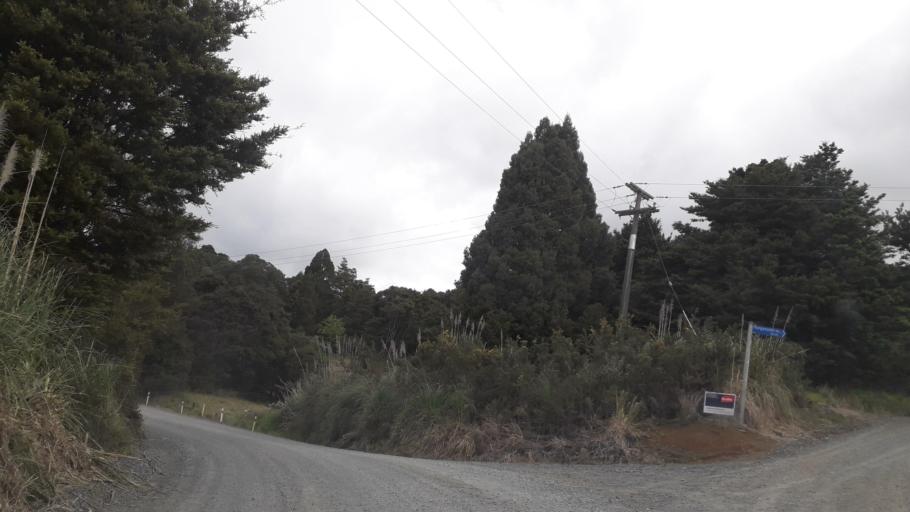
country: NZ
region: Northland
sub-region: Far North District
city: Kerikeri
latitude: -35.1180
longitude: 173.7504
